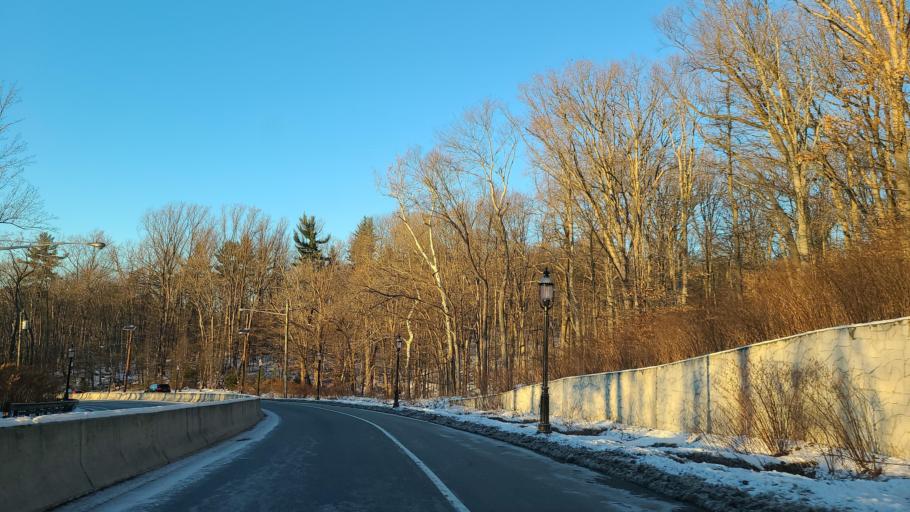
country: US
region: New Jersey
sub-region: Essex County
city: Maplewood
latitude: 40.7507
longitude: -74.2873
